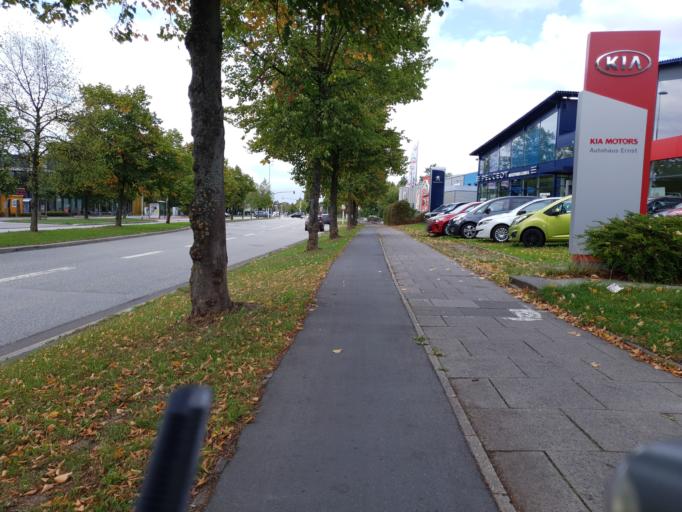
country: DE
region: Schleswig-Holstein
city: Kronshagen
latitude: 54.3520
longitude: 10.0904
